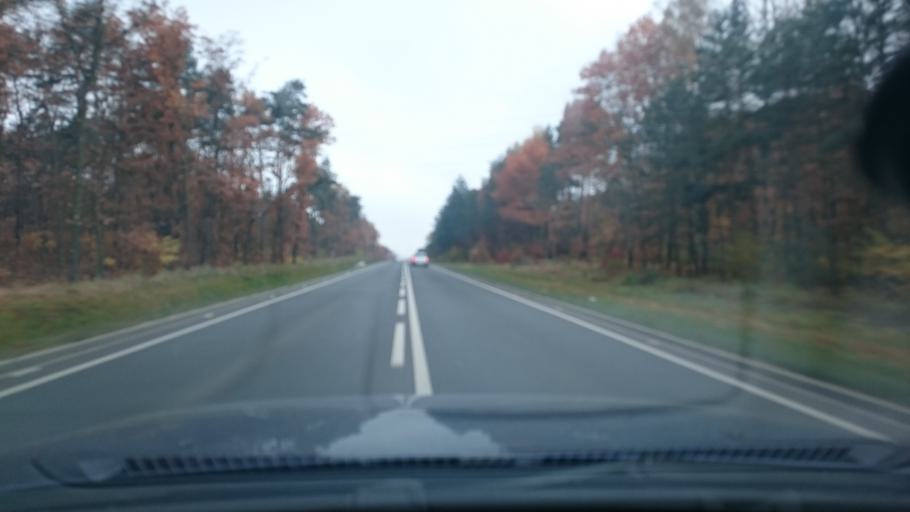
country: PL
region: Silesian Voivodeship
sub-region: Rybnik
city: Rybnik
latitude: 50.1112
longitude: 18.5620
